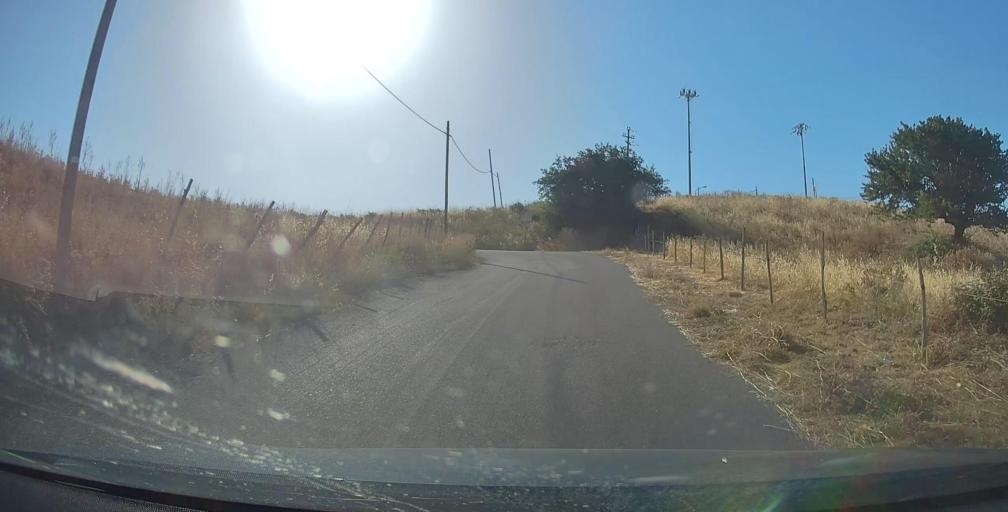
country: IT
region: Sicily
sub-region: Messina
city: San Piero Patti
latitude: 38.0756
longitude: 14.9824
